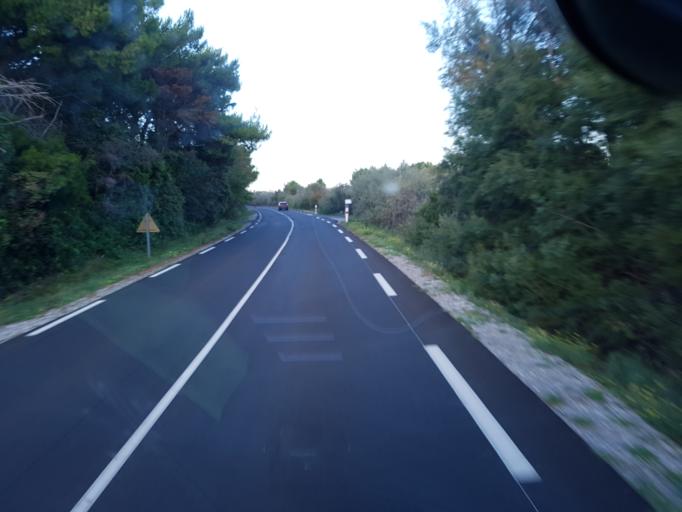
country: FR
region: Languedoc-Roussillon
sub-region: Departement de l'Aude
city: Port-la-Nouvelle
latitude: 42.9858
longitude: 3.0321
